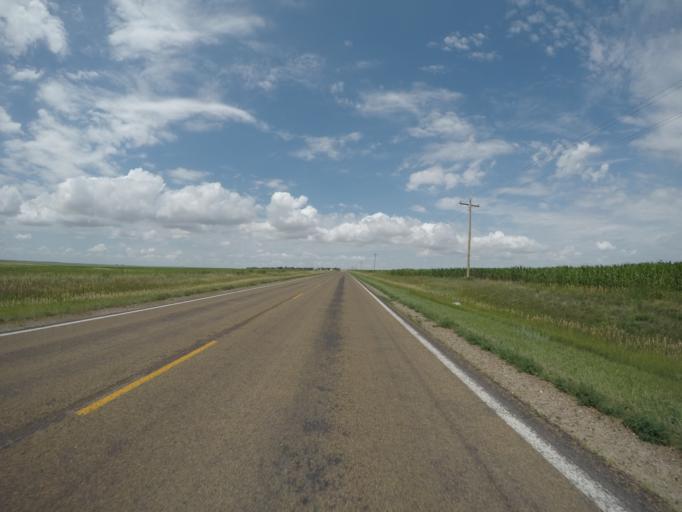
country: US
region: Kansas
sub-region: Rawlins County
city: Atwood
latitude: 39.8508
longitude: -101.0467
